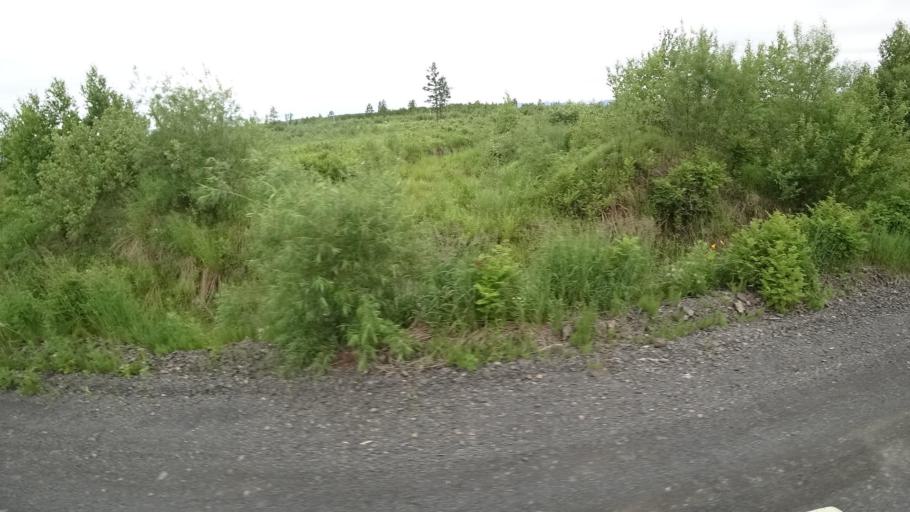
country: RU
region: Khabarovsk Krai
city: Amursk
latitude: 49.9073
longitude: 136.1474
